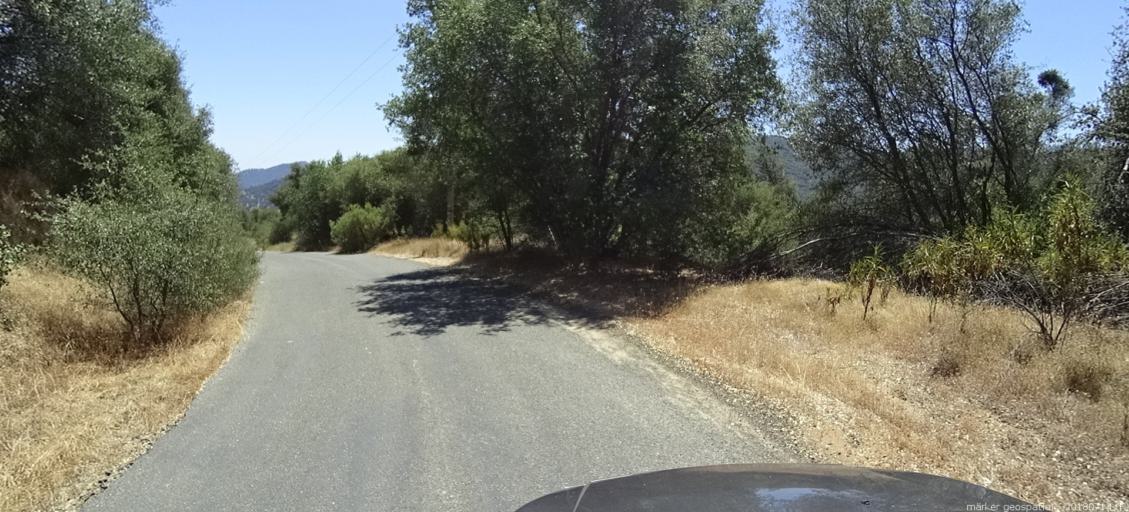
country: US
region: California
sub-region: Madera County
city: Ahwahnee
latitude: 37.3841
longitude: -119.7404
